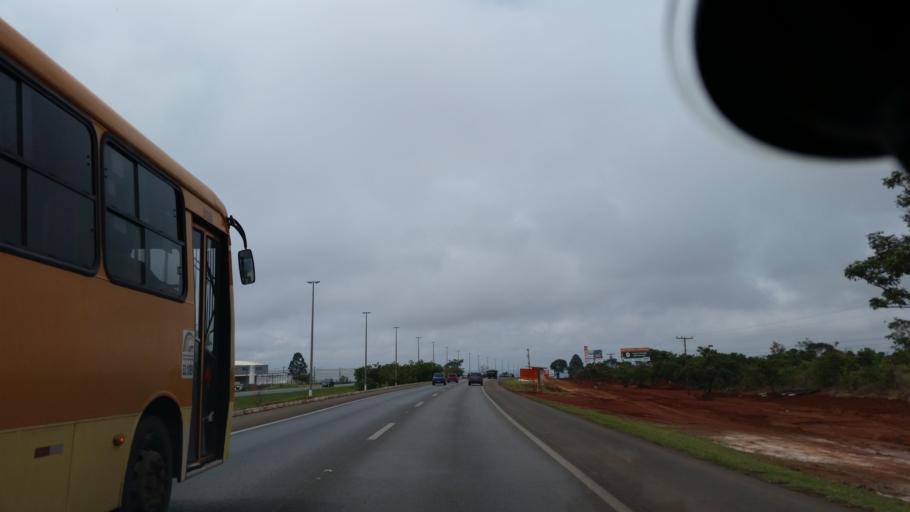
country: BR
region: Goias
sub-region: Luziania
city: Luziania
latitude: -16.0309
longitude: -47.9789
